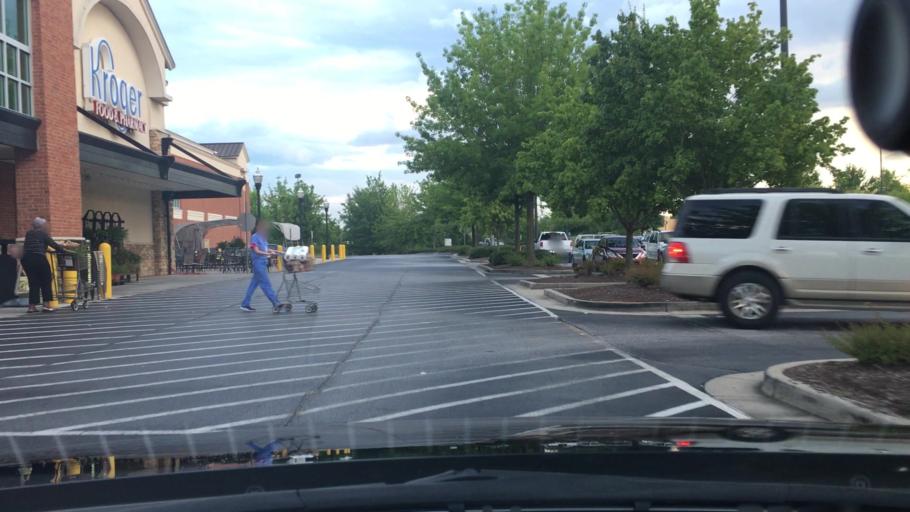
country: US
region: Georgia
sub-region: Coweta County
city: East Newnan
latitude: 33.3774
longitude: -84.7522
